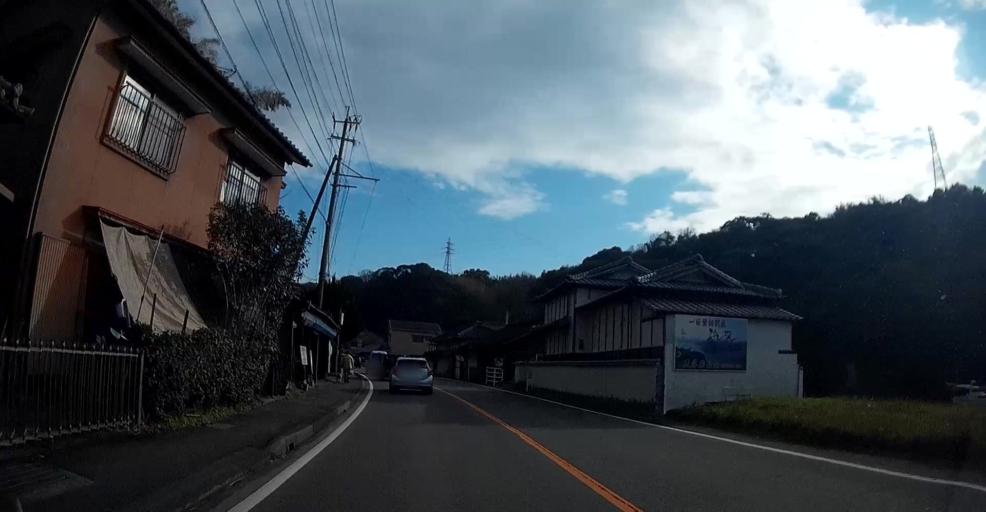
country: JP
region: Kumamoto
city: Yatsushiro
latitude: 32.6131
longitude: 130.4624
